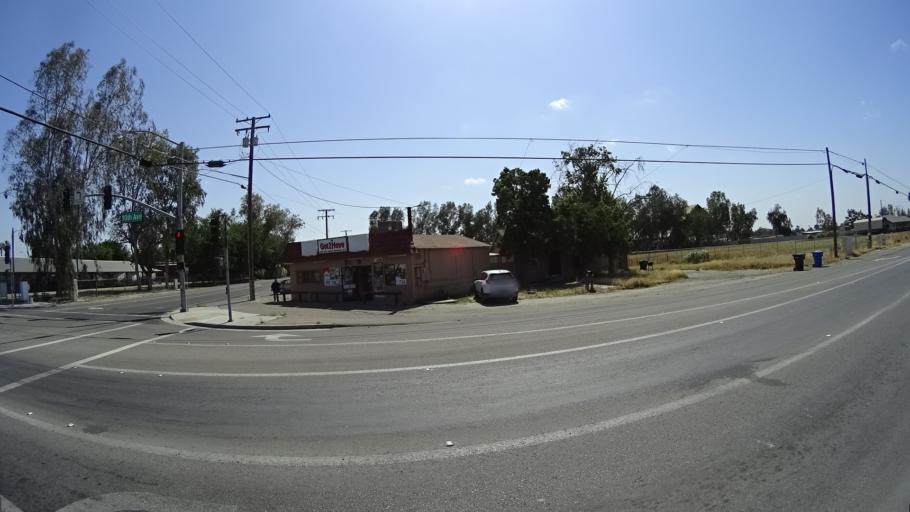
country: US
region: California
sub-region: Kings County
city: Home Garden
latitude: 36.3132
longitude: -119.6371
